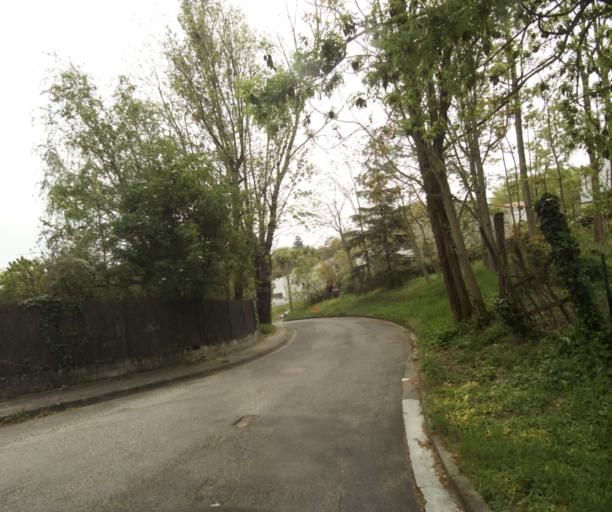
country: FR
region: Midi-Pyrenees
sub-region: Departement de la Haute-Garonne
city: Pechabou
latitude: 43.5033
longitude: 1.5073
